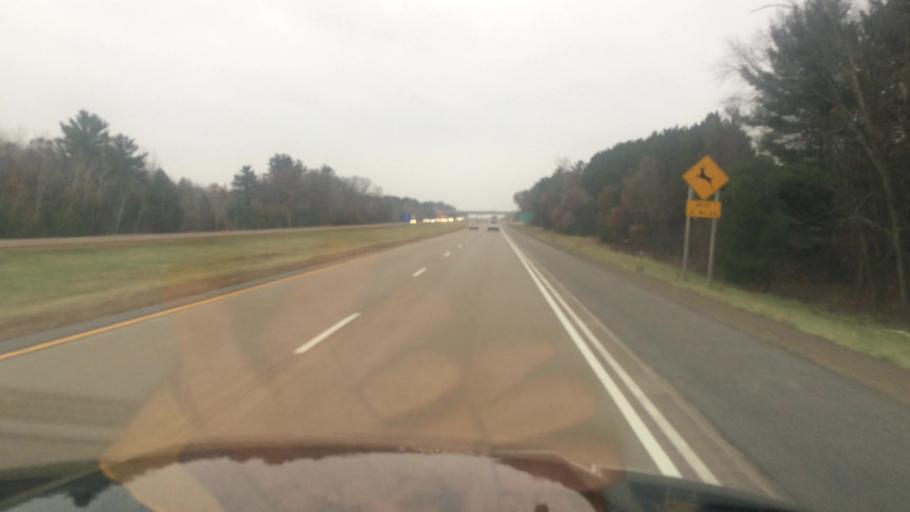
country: US
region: Wisconsin
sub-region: Portage County
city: Stevens Point
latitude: 44.6053
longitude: -89.6200
